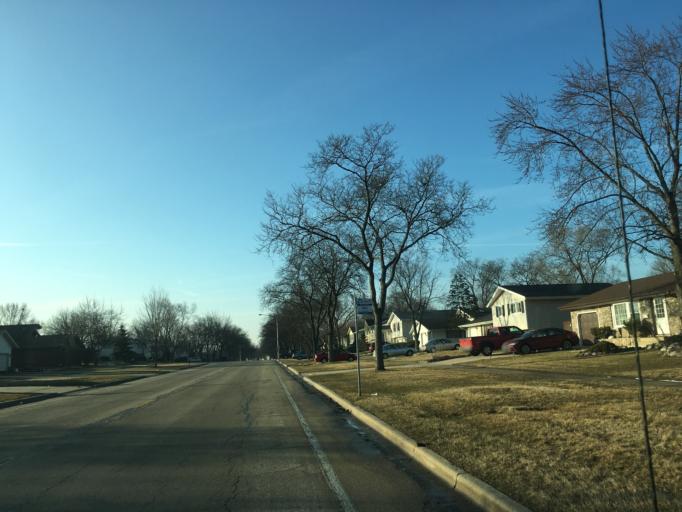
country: US
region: Illinois
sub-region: Cook County
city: Schaumburg
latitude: 42.0235
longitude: -88.1002
